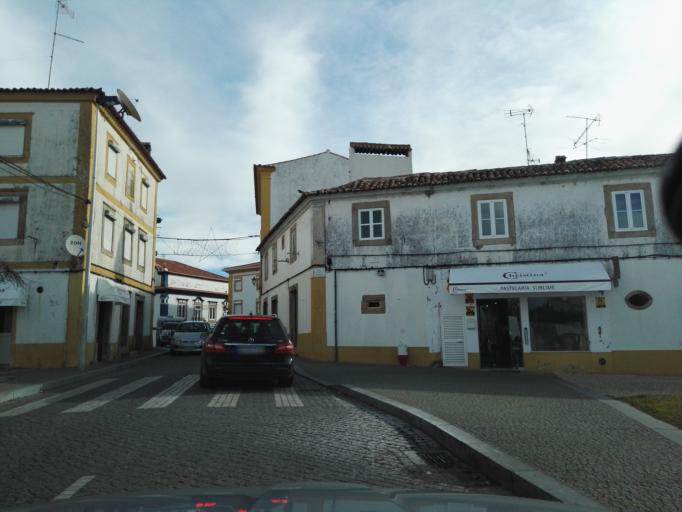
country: PT
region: Portalegre
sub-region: Nisa
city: Nisa
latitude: 39.5168
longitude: -7.6493
